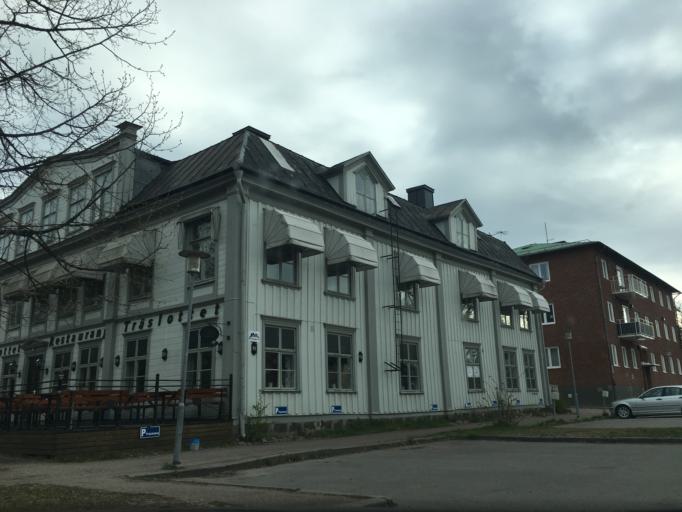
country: SE
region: Vaermland
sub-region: Kristinehamns Kommun
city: Kristinehamn
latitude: 59.3138
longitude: 14.1081
